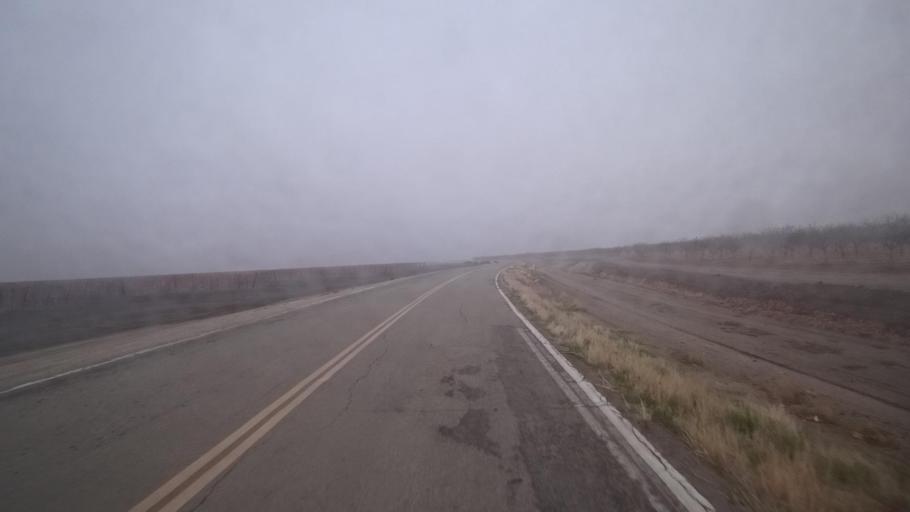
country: US
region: California
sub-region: Kern County
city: Buttonwillow
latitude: 35.4213
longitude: -119.5232
